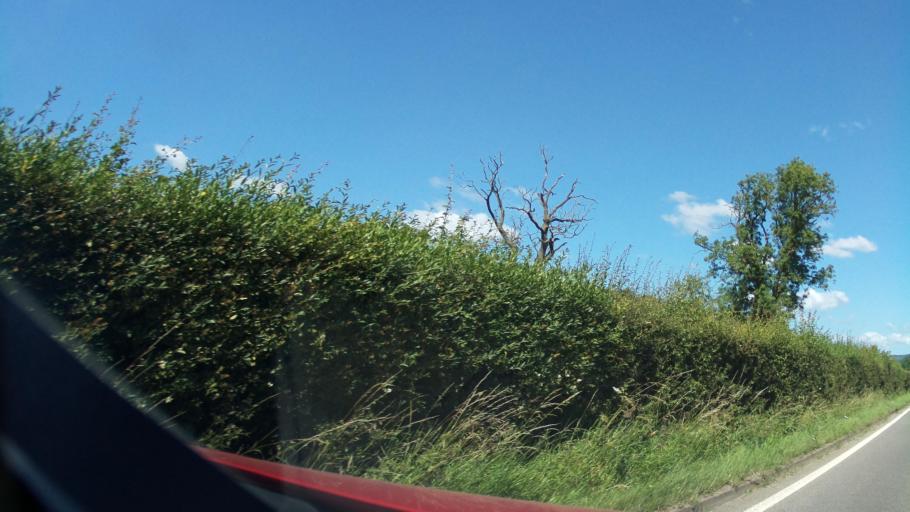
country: GB
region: England
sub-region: Derbyshire
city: Bakewell
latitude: 53.1996
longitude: -1.6614
